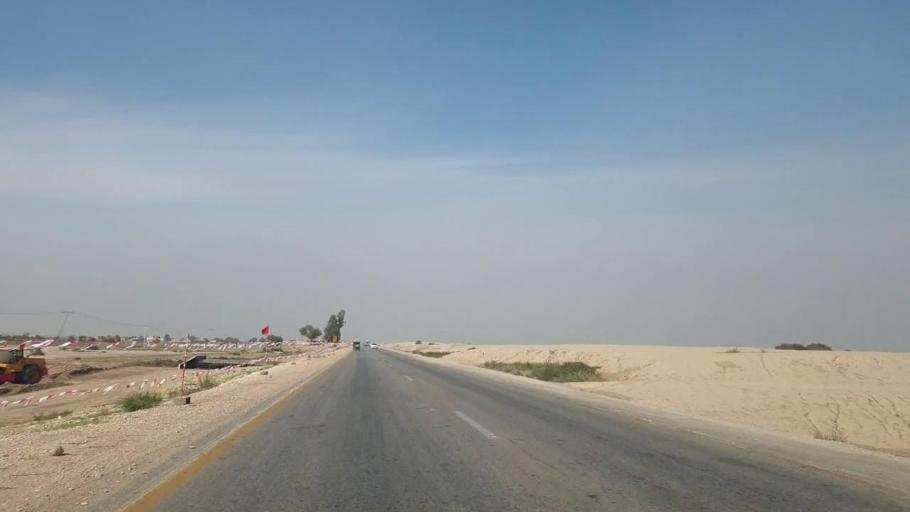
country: PK
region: Sindh
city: Sann
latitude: 25.9609
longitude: 68.1922
